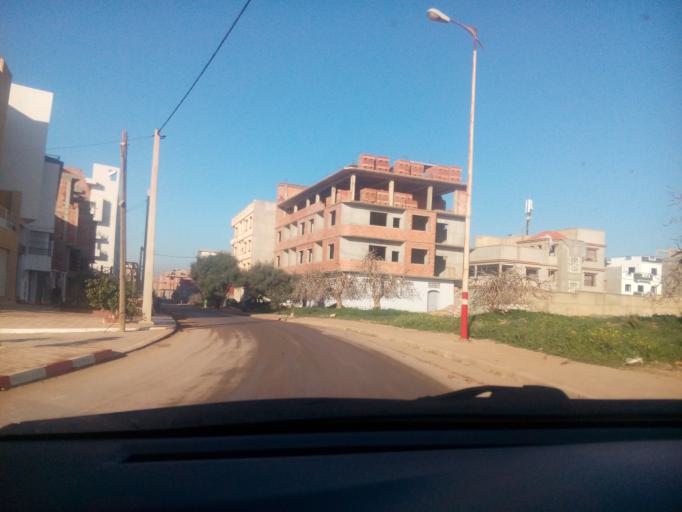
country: DZ
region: Oran
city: Bir el Djir
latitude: 35.7554
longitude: -0.5306
